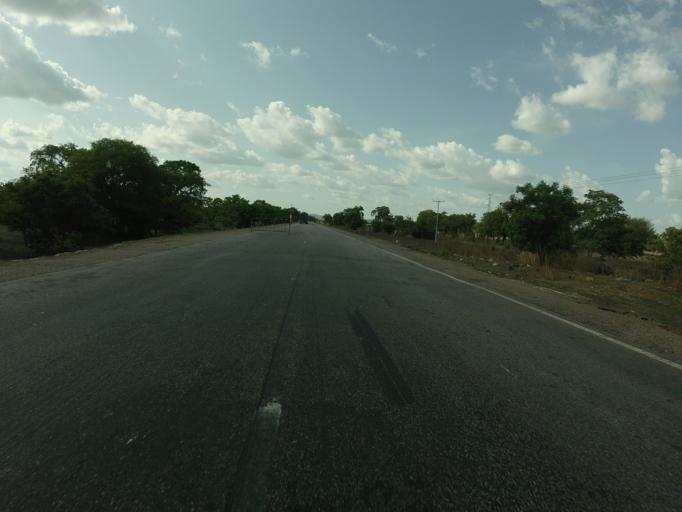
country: GH
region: Upper East
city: Bolgatanga
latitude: 10.5766
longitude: -0.8325
